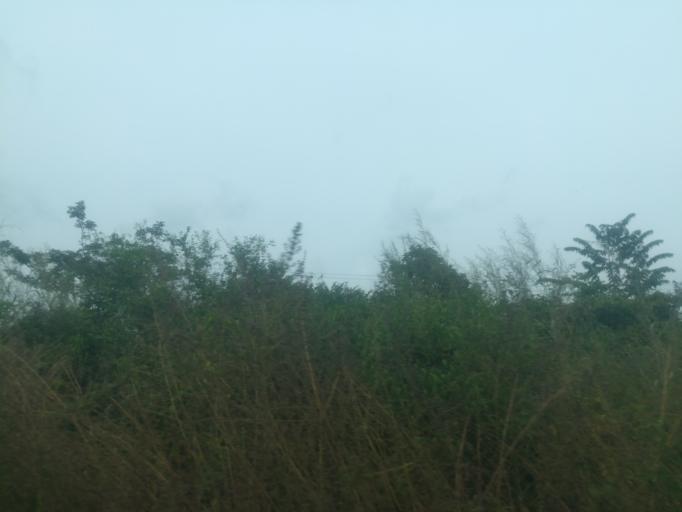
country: NG
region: Ogun
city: Ayetoro
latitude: 7.3464
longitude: 3.0564
